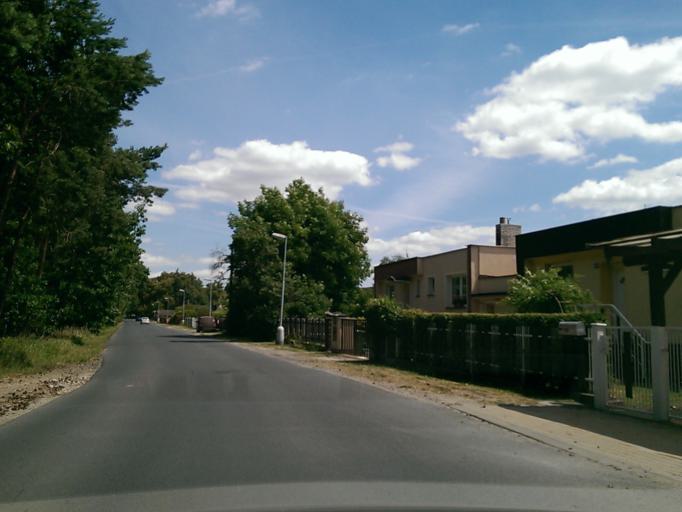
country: CZ
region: Central Bohemia
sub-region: Okres Melnik
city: Melnik
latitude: 50.3739
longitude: 14.5029
